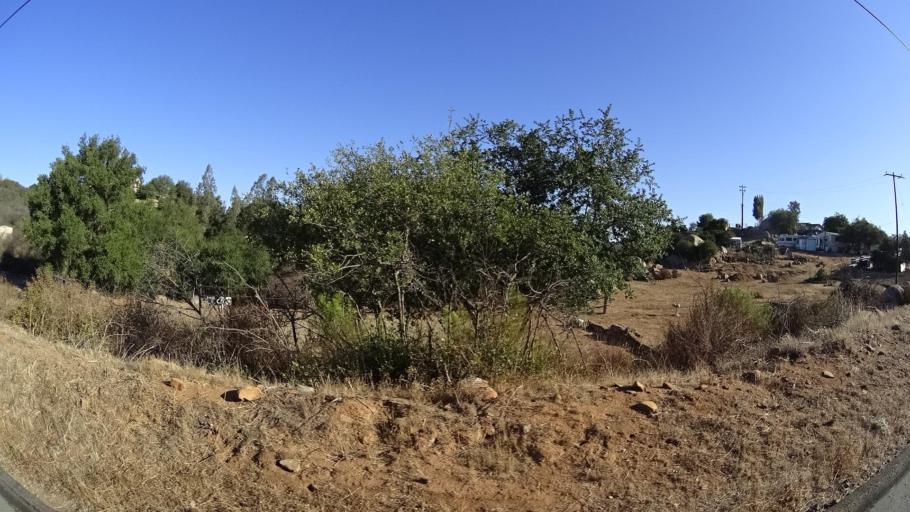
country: US
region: California
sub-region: San Diego County
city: Eucalyptus Hills
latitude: 32.9055
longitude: -116.9053
